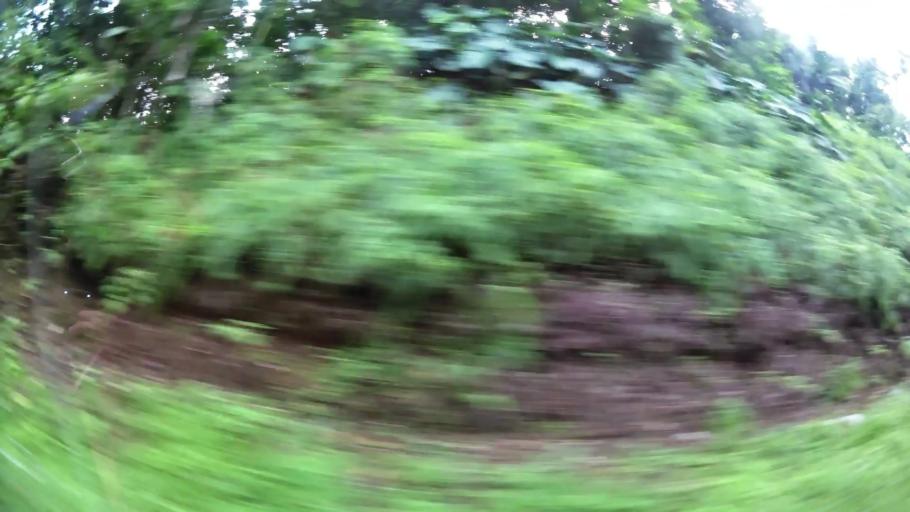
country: GP
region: Guadeloupe
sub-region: Guadeloupe
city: Bouillante
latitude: 16.1795
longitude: -61.7125
